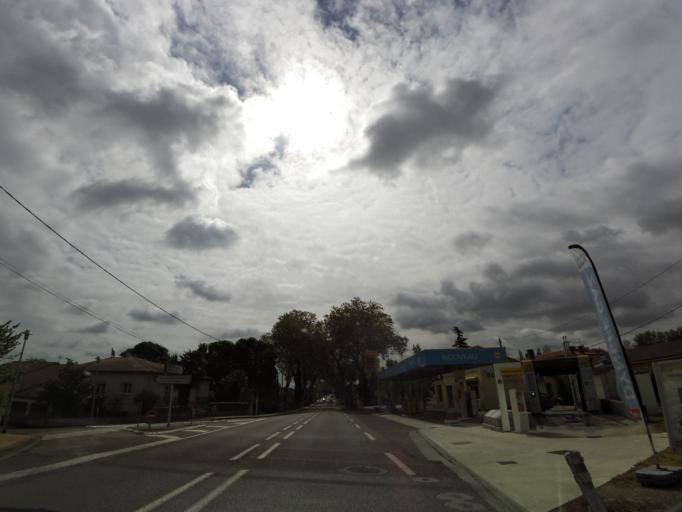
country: FR
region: Languedoc-Roussillon
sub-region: Departement de l'Aude
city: Castelnaudary
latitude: 43.3134
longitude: 1.9653
